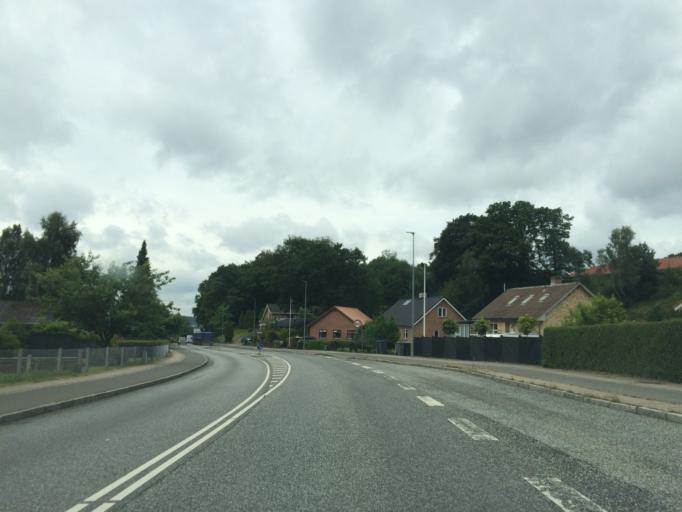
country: DK
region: Central Jutland
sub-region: Silkeborg Kommune
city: Silkeborg
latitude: 56.1952
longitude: 9.5844
